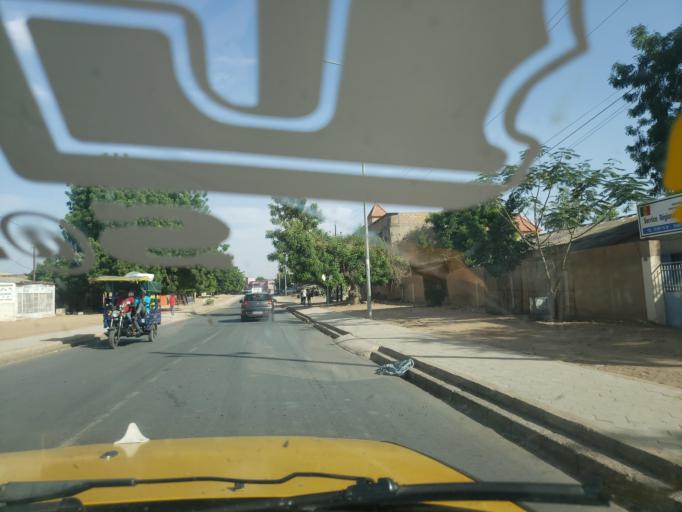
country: SN
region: Louga
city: Louga
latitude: 15.6224
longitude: -16.2130
